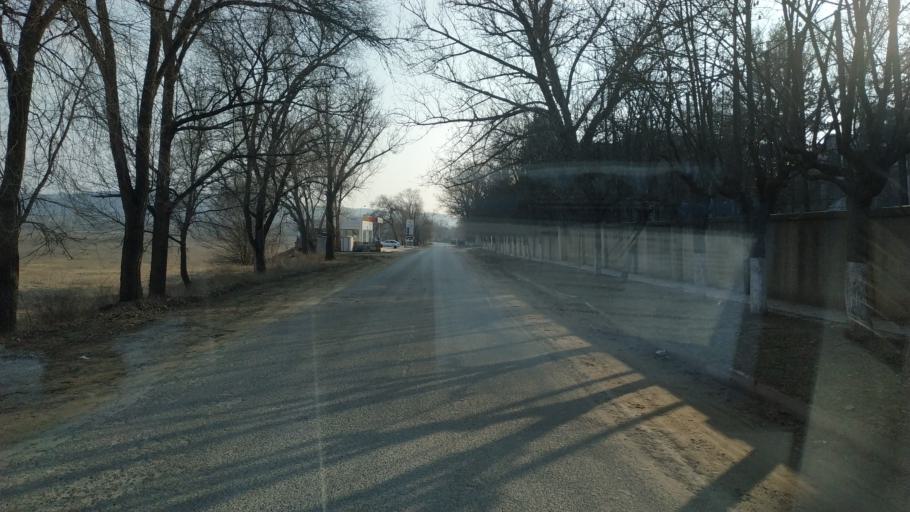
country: MD
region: Hincesti
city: Dancu
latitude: 46.7699
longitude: 28.3462
